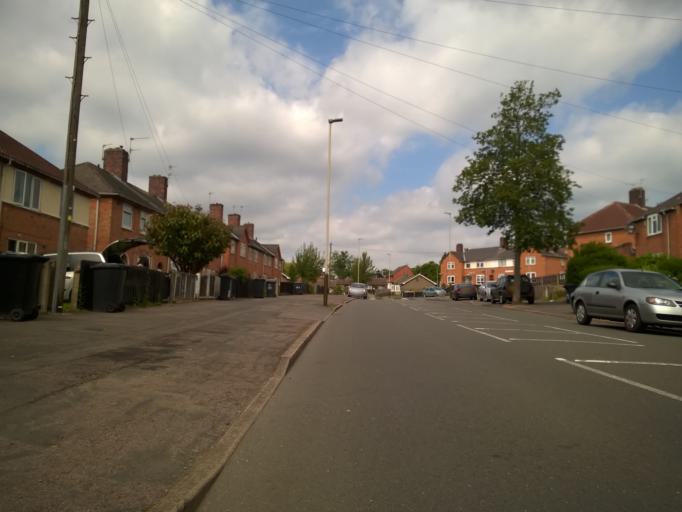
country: GB
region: England
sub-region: City of Leicester
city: Leicester
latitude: 52.6423
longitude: -1.1576
